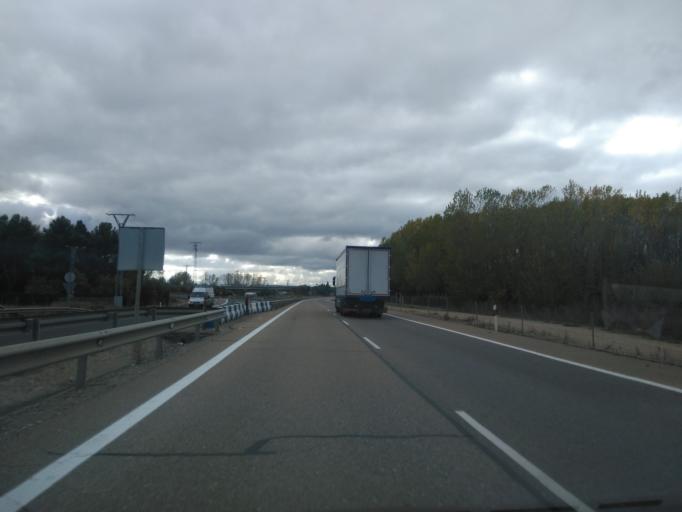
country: ES
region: Castille and Leon
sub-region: Provincia de Palencia
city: Venta de Banos
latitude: 41.9327
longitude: -4.5031
